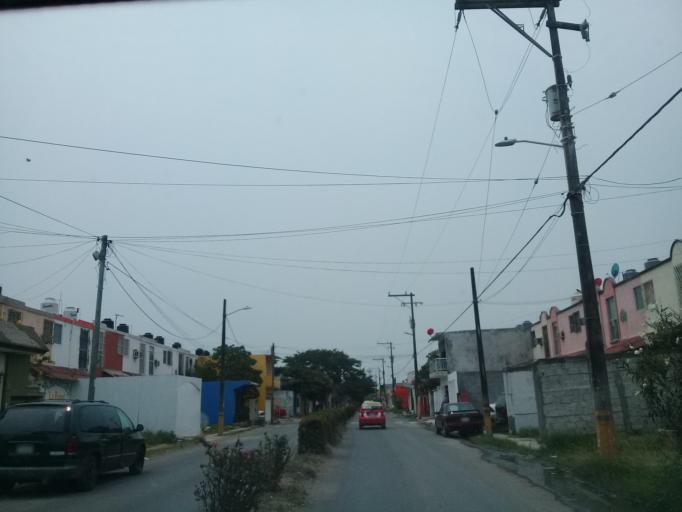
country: MX
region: Veracruz
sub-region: Veracruz
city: Las Amapolas
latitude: 19.1563
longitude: -96.2061
